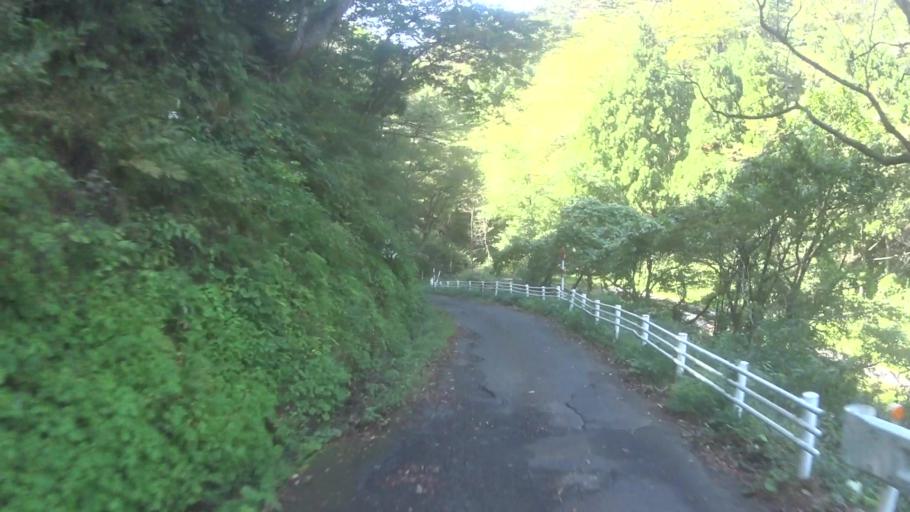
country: JP
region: Kyoto
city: Miyazu
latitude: 35.6562
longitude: 135.1583
